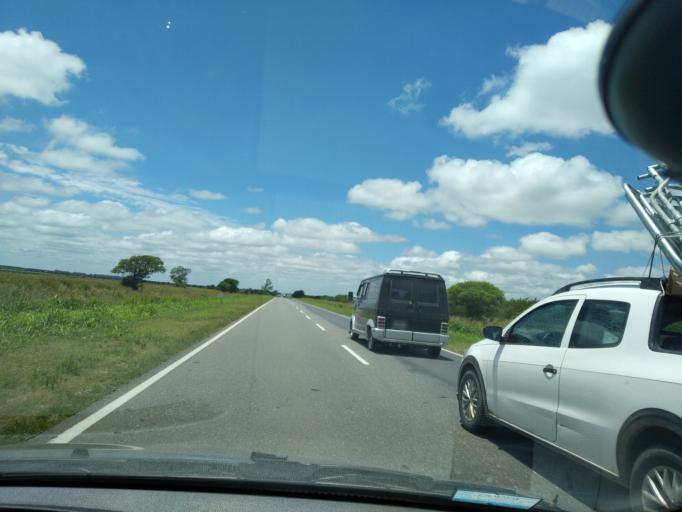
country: AR
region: Cordoba
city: Despenaderos
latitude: -31.6520
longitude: -64.2138
